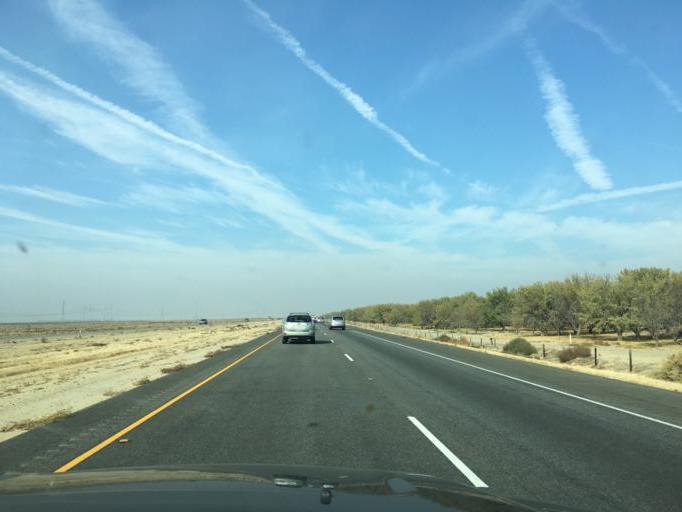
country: US
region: California
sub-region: Kern County
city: Buttonwillow
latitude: 35.4782
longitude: -119.5060
